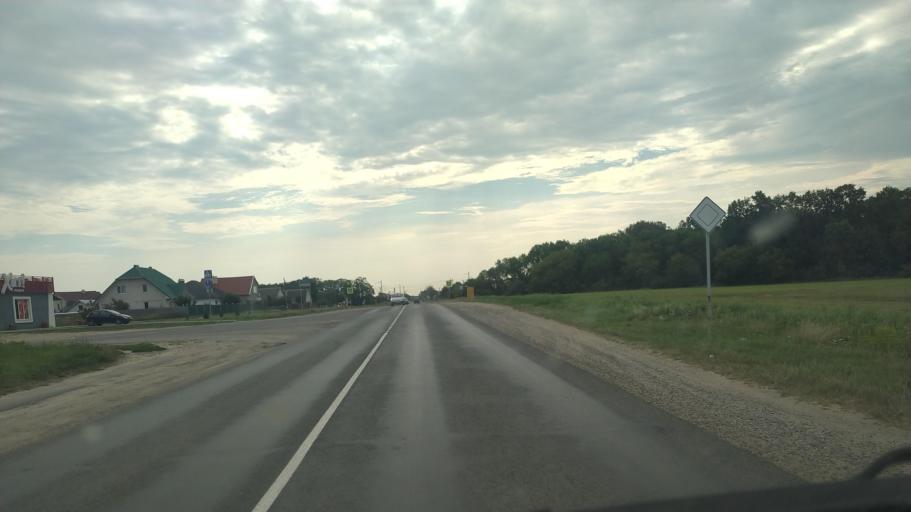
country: BY
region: Brest
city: Byaroza
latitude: 52.5464
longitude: 24.9556
